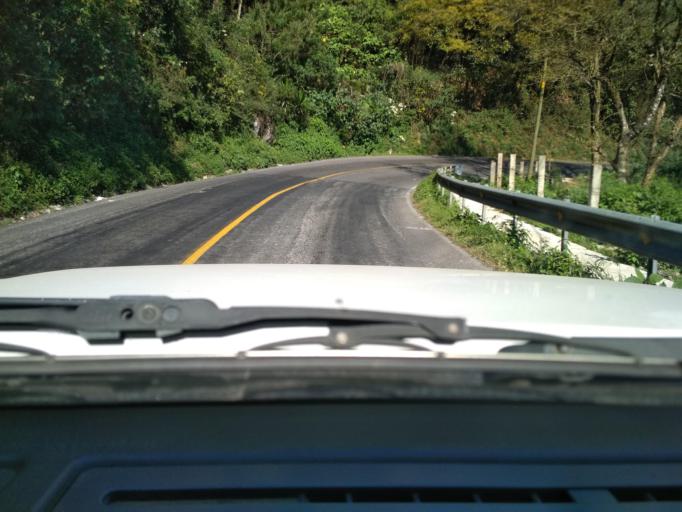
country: MX
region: Veracruz
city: Tequila
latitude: 18.7498
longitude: -97.0911
